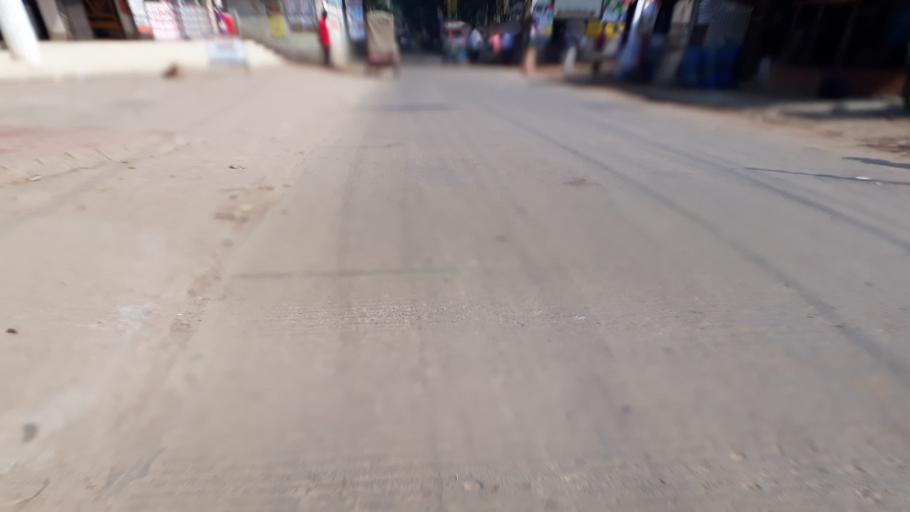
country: BD
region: Dhaka
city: Tungi
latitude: 23.8885
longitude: 90.3181
